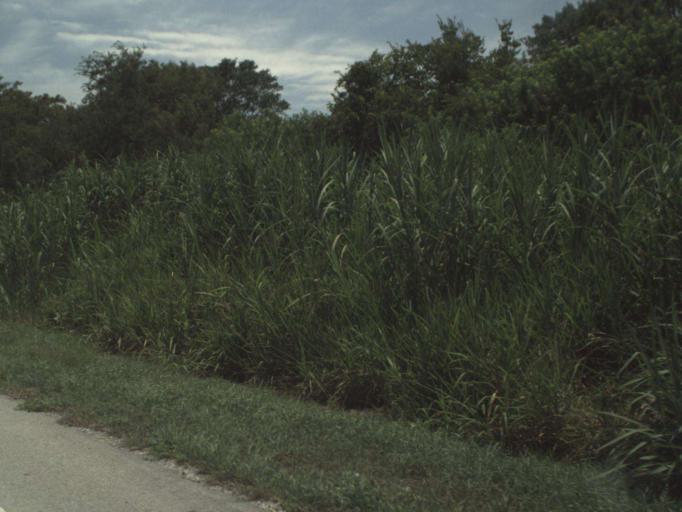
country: US
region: Florida
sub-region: Martin County
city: Indiantown
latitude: 27.0109
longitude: -80.6261
